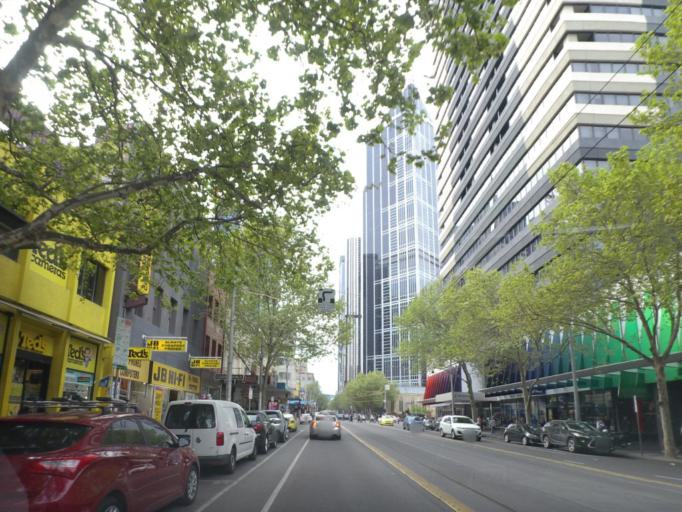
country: AU
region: Victoria
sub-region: Melbourne
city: Melbourne
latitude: -37.8132
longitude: 144.9627
